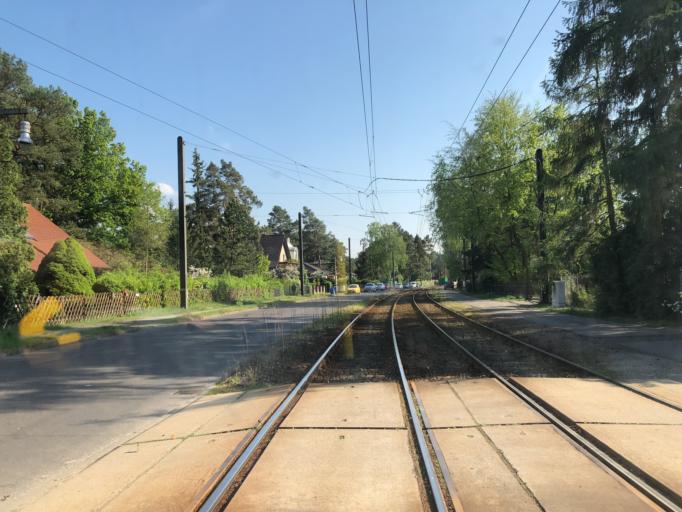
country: DE
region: Berlin
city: Schmockwitz
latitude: 52.3900
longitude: 13.6352
